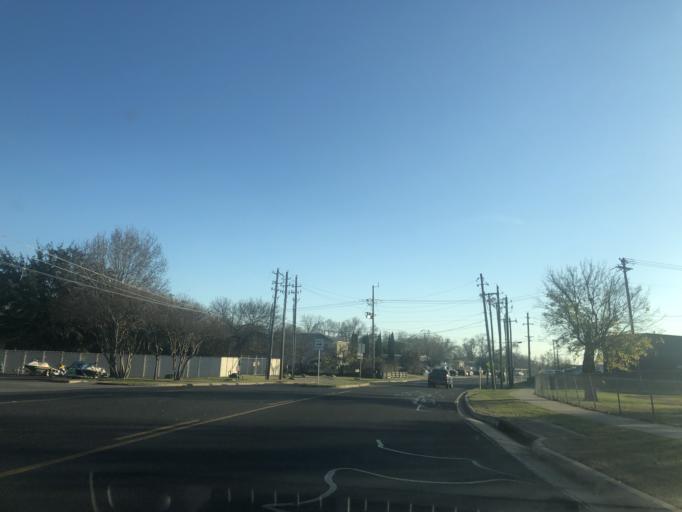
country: US
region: Texas
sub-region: Travis County
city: Wells Branch
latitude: 30.4309
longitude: -97.6748
